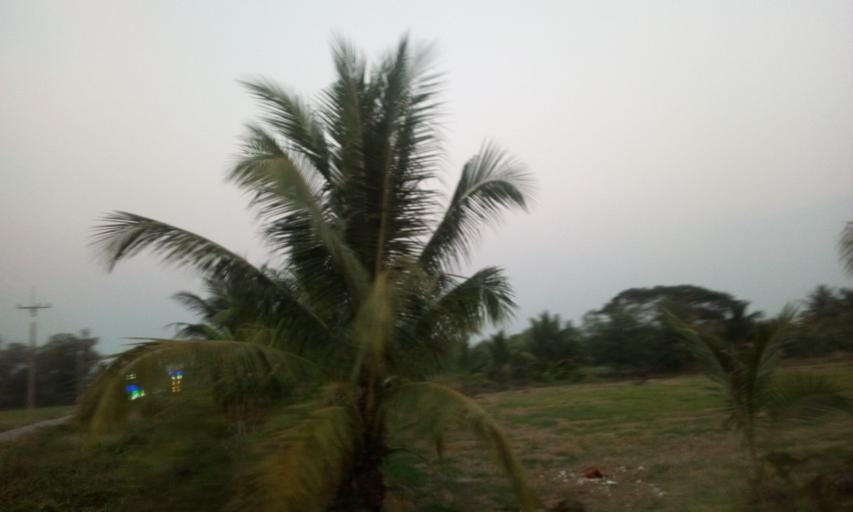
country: TH
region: Sing Buri
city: Sing Buri
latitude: 14.8335
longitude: 100.3995
